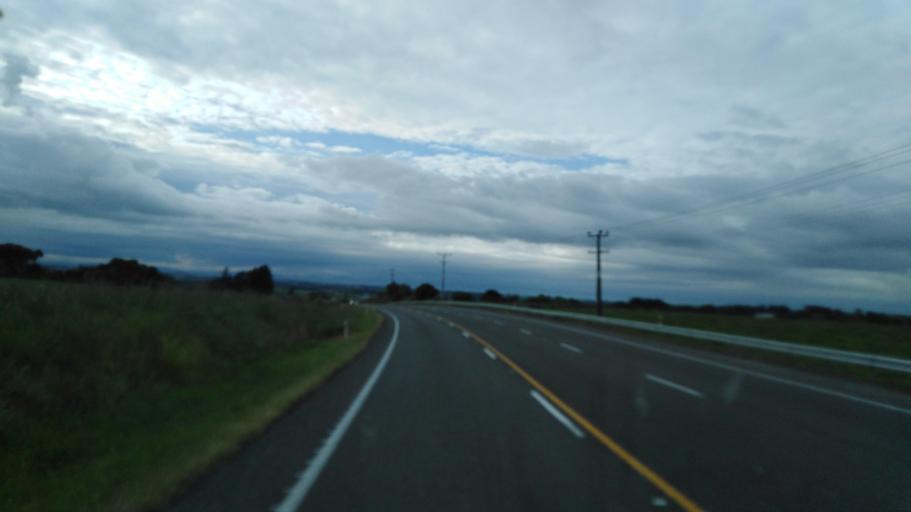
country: NZ
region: Manawatu-Wanganui
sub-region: Rangitikei District
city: Bulls
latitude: -40.1448
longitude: 175.3688
